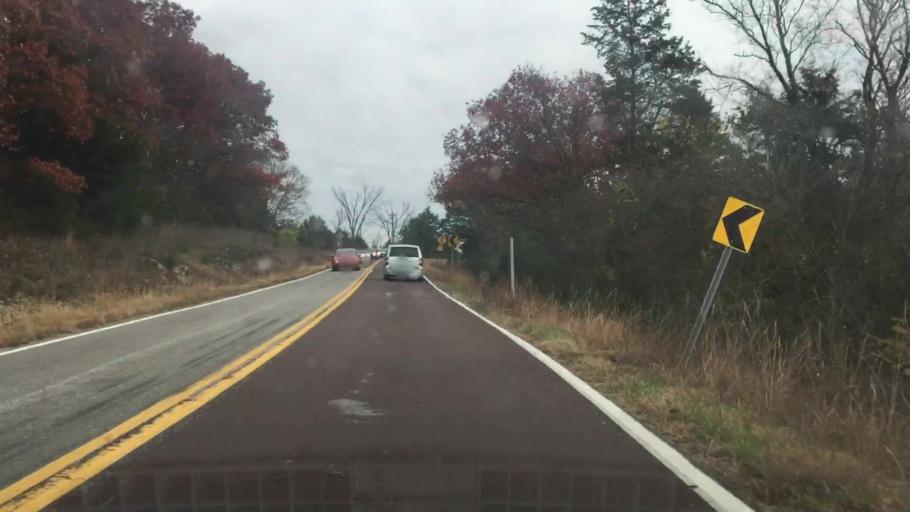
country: US
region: Missouri
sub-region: Callaway County
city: Fulton
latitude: 38.7781
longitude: -91.8470
